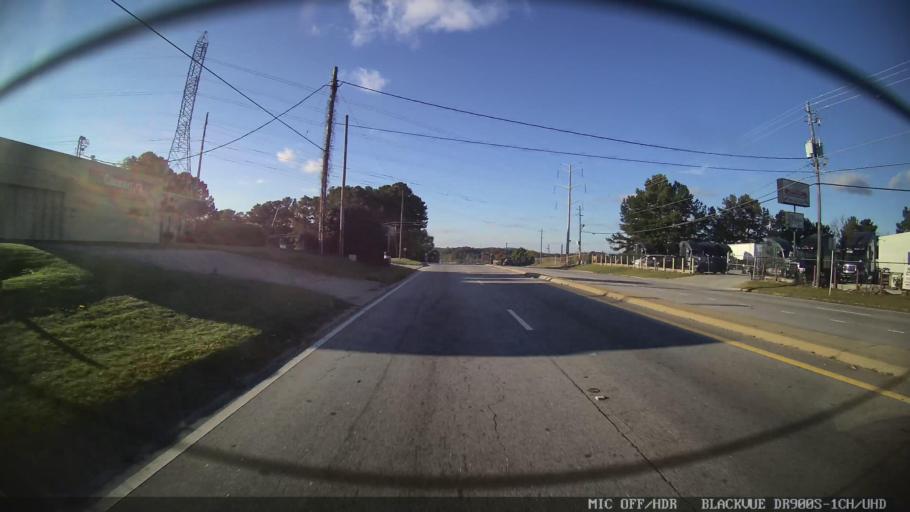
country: US
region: Georgia
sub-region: Clayton County
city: Conley
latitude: 33.6391
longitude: -84.3212
